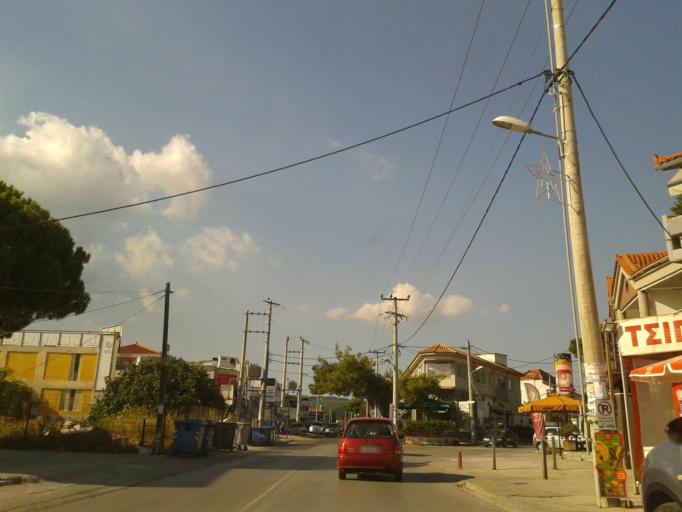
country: GR
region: Attica
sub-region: Nomarchia Anatolikis Attikis
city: Anoixi
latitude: 38.1376
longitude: 23.8555
